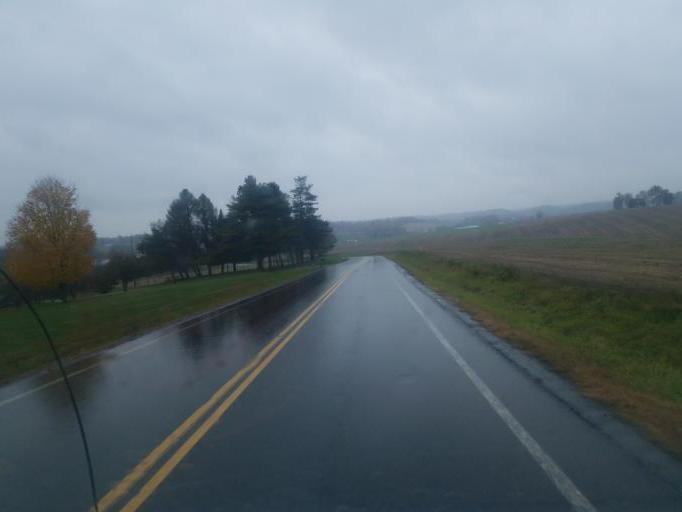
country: US
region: Ohio
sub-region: Licking County
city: Utica
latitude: 40.2622
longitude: -82.3464
